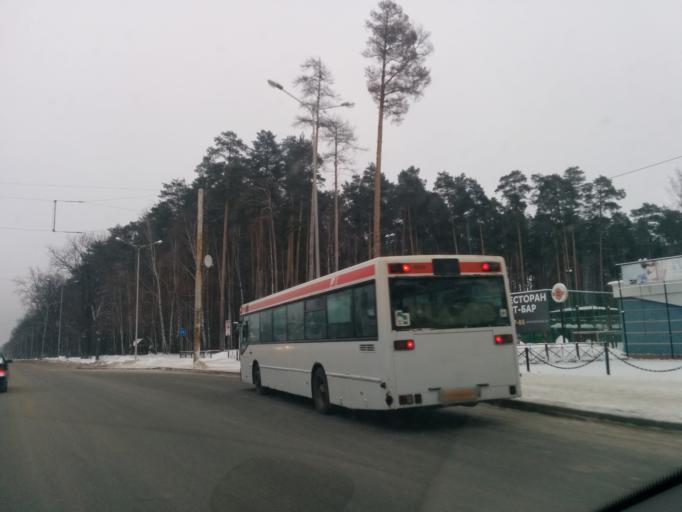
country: RU
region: Perm
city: Kultayevo
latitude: 58.0114
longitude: 55.9691
